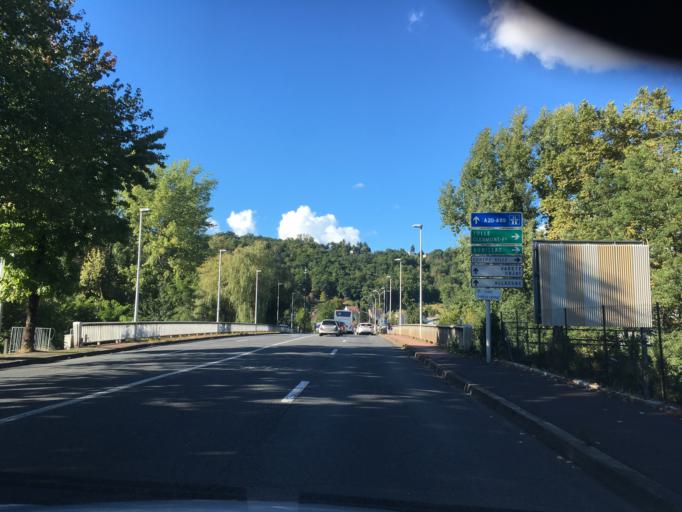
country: FR
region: Limousin
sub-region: Departement de la Correze
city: Brive-la-Gaillarde
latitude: 45.1618
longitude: 1.5031
